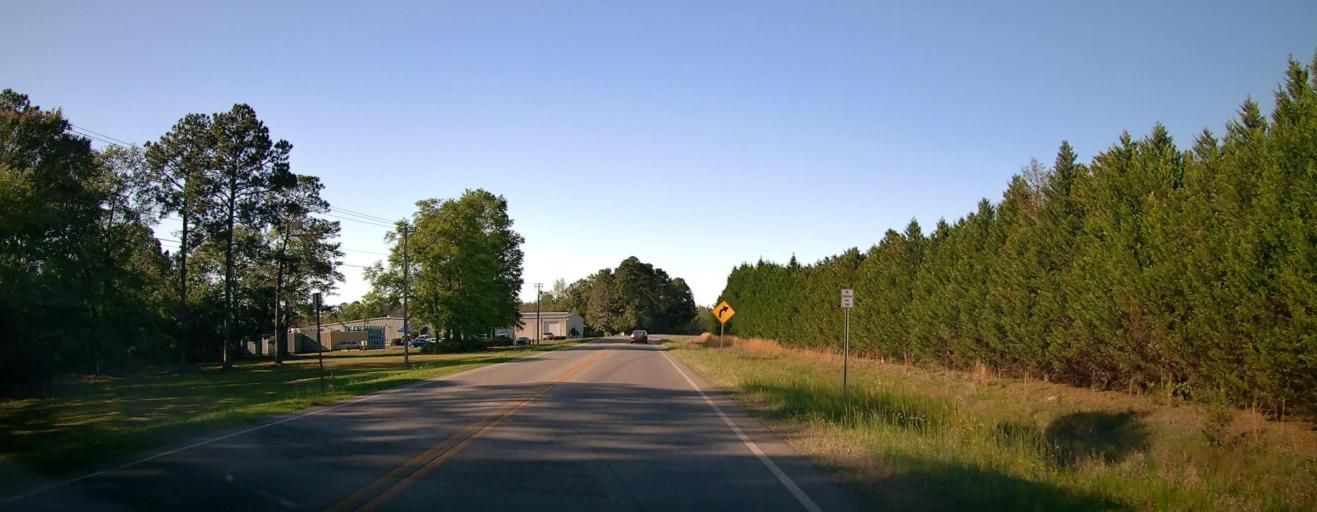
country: US
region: Georgia
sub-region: Ben Hill County
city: Fitzgerald
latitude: 31.7014
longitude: -83.2394
